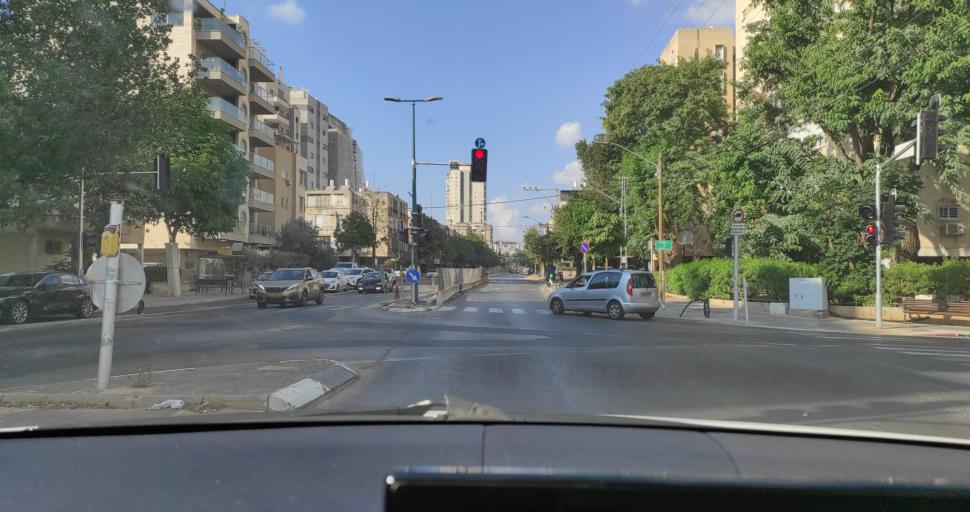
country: IL
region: Tel Aviv
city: Bene Beraq
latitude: 32.0662
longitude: 34.8284
